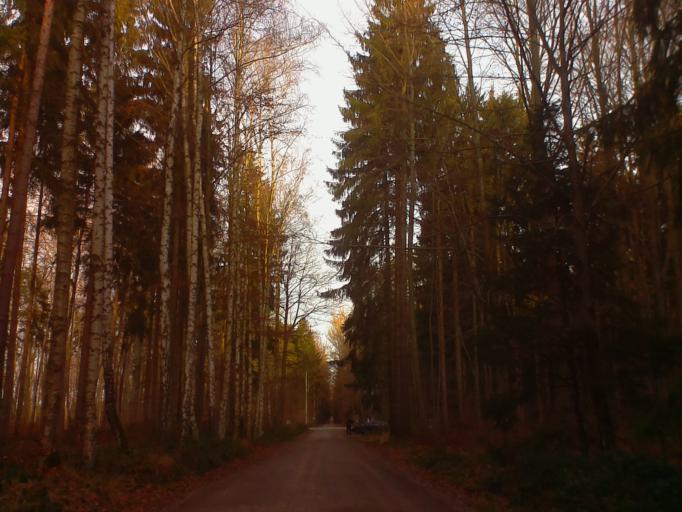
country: DE
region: Thuringia
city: Hummelshain
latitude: 50.7635
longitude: 11.6457
